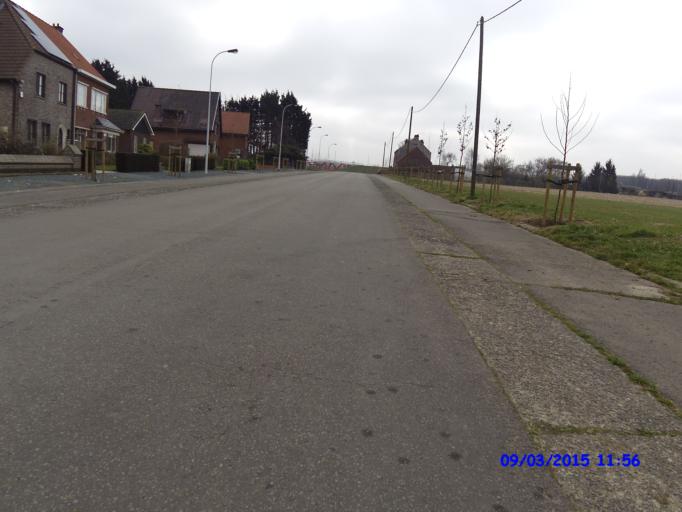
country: BE
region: Flanders
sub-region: Provincie Vlaams-Brabant
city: Machelen
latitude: 50.9185
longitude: 4.4551
